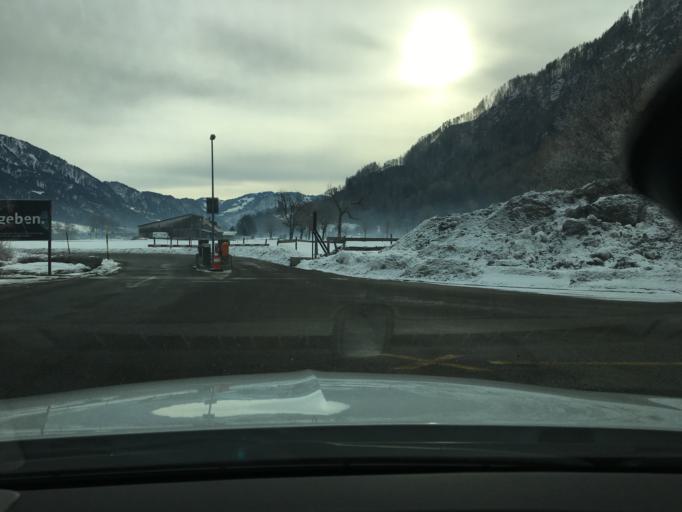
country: CH
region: Saint Gallen
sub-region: Wahlkreis Sarganserland
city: Bad Ragaz
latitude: 47.0167
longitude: 9.4754
